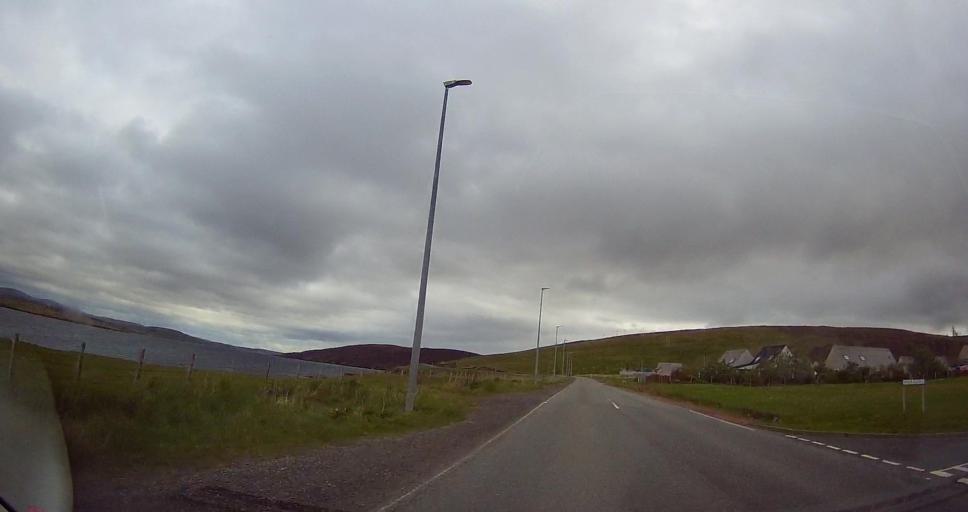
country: GB
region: Scotland
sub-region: Shetland Islands
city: Lerwick
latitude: 60.3985
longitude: -1.3538
